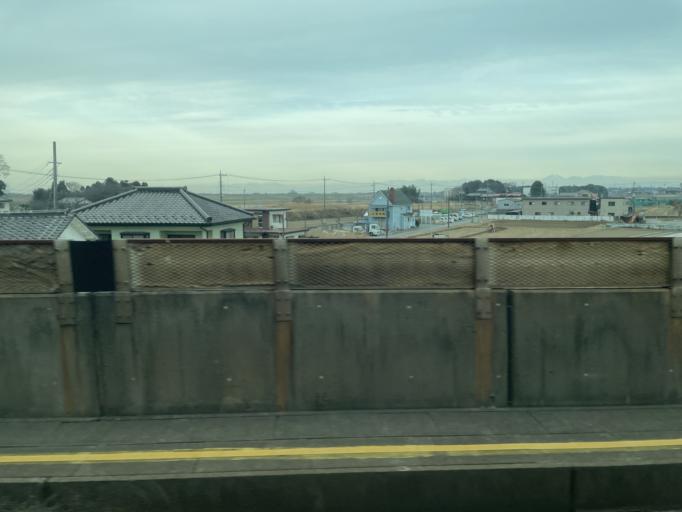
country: JP
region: Saitama
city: Kurihashi
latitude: 36.1519
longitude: 139.7082
